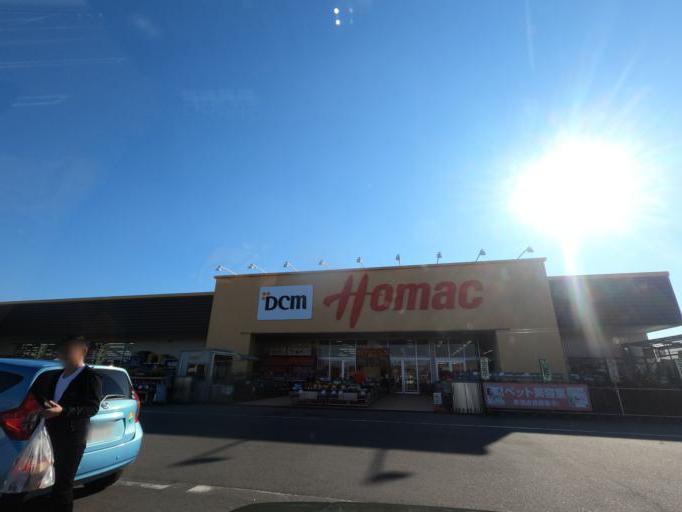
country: JP
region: Ibaraki
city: Mitsukaido
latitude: 35.9754
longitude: 139.9737
